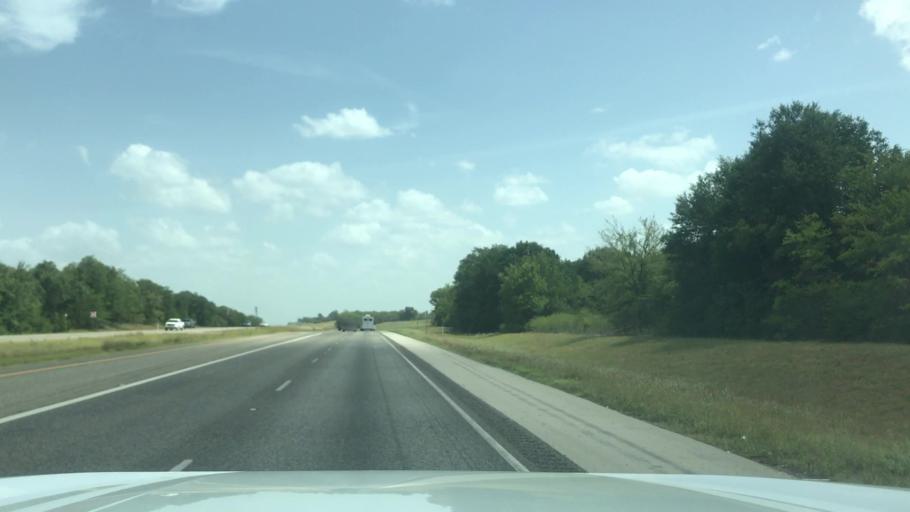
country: US
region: Texas
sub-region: Robertson County
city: Calvert
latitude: 30.9378
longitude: -96.6402
